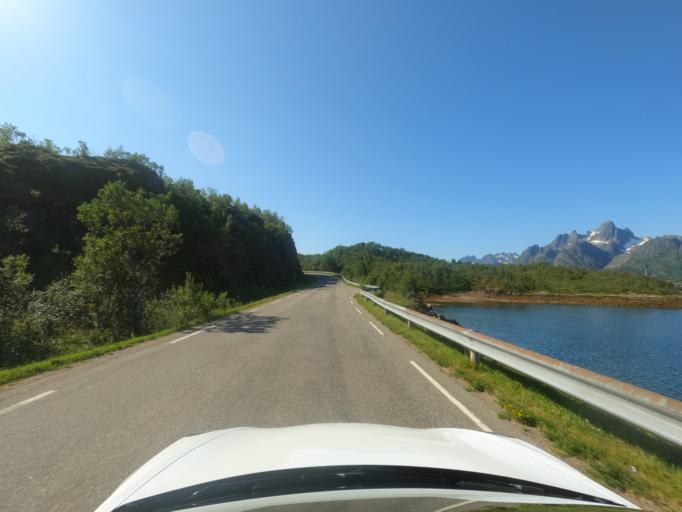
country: NO
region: Nordland
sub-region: Hadsel
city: Stokmarknes
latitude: 68.3537
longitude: 15.0700
